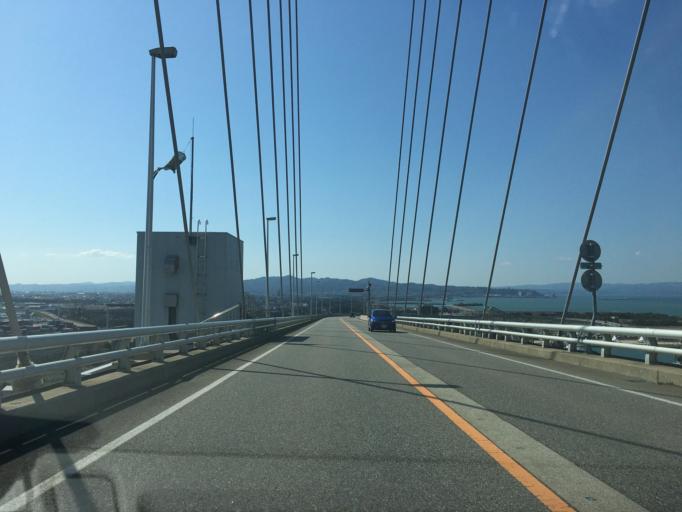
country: JP
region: Toyama
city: Nishishinminato
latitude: 36.7763
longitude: 137.1134
